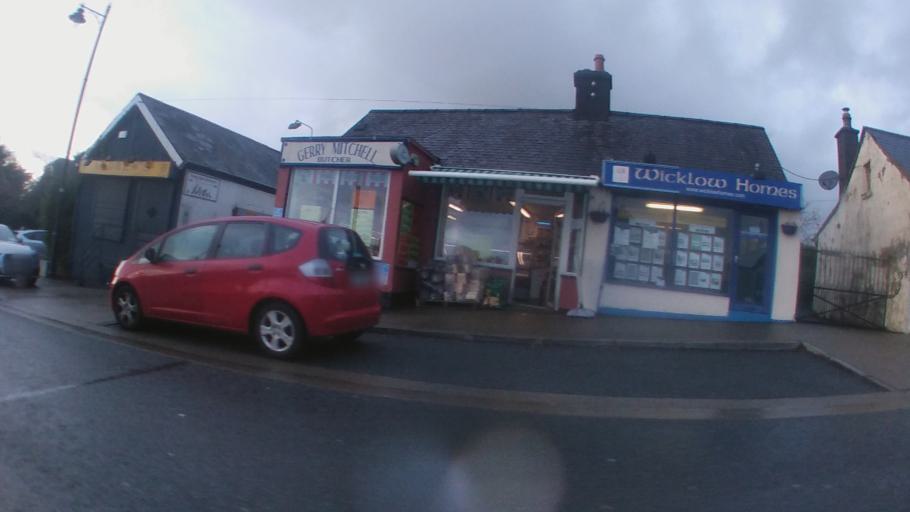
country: IE
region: Leinster
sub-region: Wicklow
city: Kilcoole
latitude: 53.1082
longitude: -6.0647
